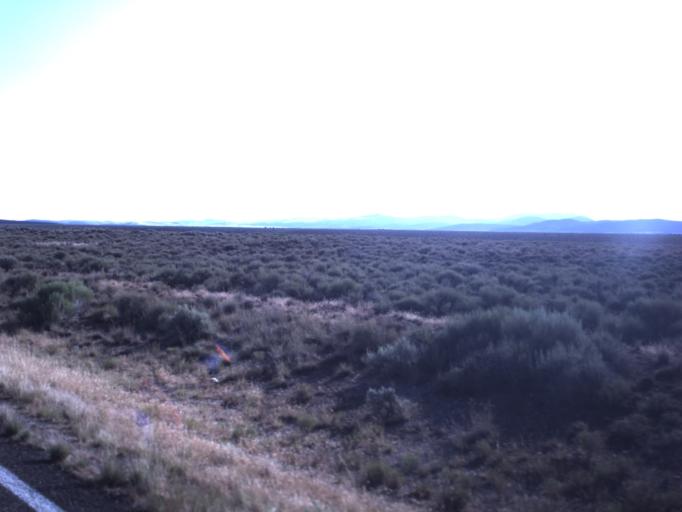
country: US
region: Utah
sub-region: Iron County
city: Enoch
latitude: 37.9830
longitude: -113.0028
